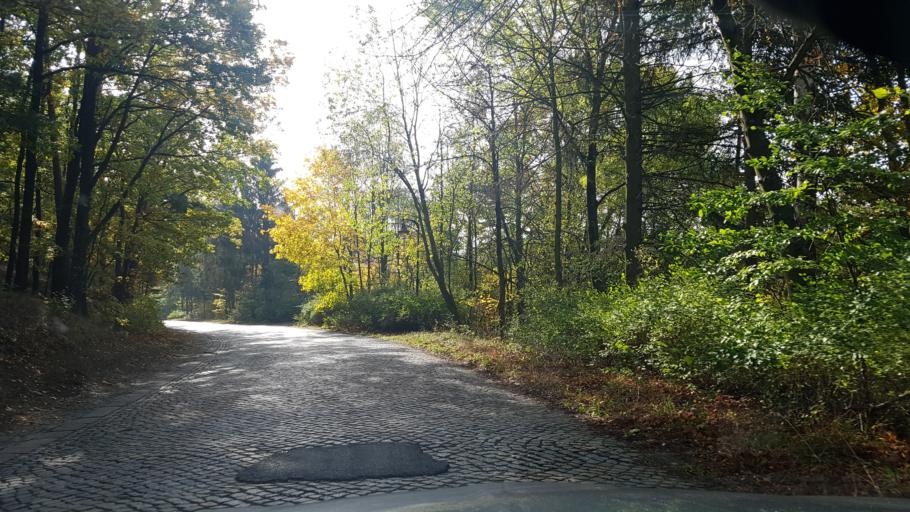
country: DE
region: Saxony
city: Struppen
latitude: 50.9091
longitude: 14.0274
